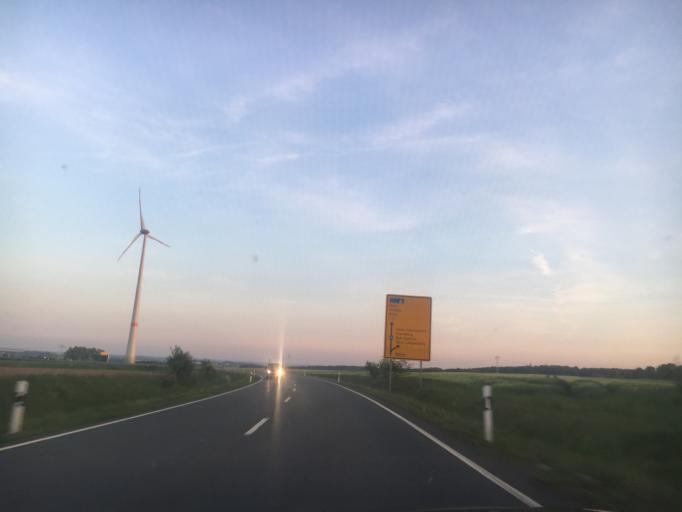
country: DE
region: Thuringia
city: Schwaara
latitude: 50.9451
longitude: 12.1108
